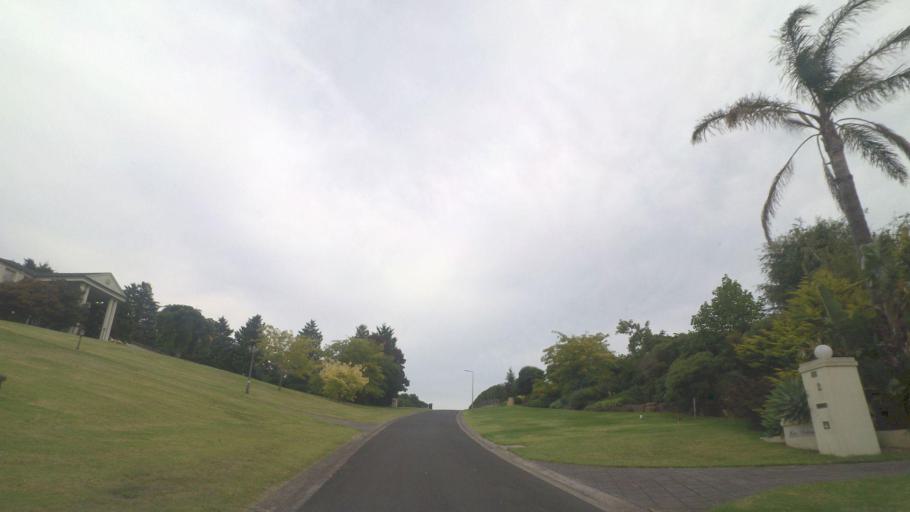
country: AU
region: Victoria
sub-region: Manningham
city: Park Orchards
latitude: -37.7534
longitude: 145.1933
